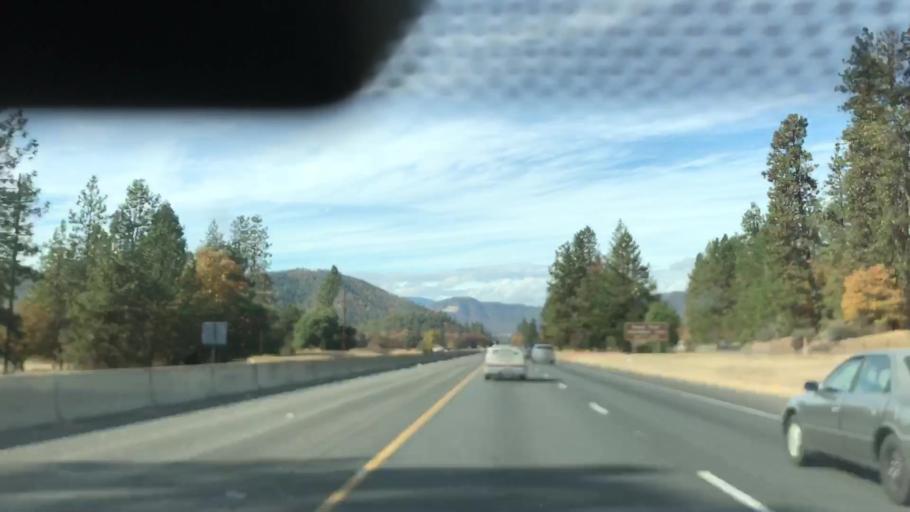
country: US
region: Oregon
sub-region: Jackson County
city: Gold Hill
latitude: 42.4188
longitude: -123.0144
